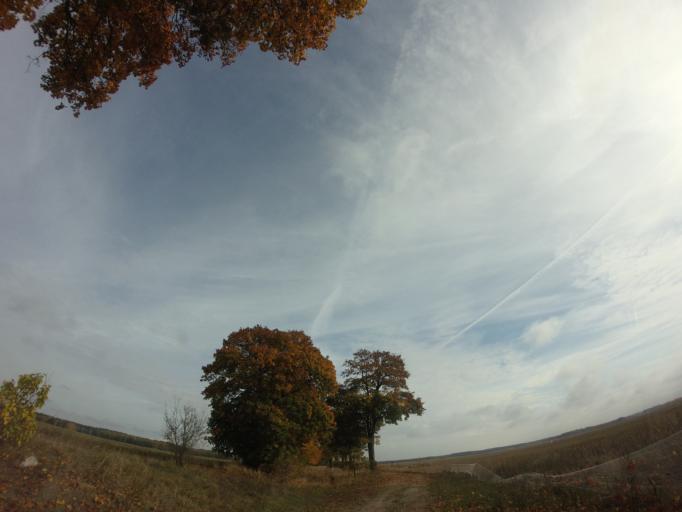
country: PL
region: West Pomeranian Voivodeship
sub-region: Powiat choszczenski
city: Recz
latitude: 53.2613
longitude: 15.6293
